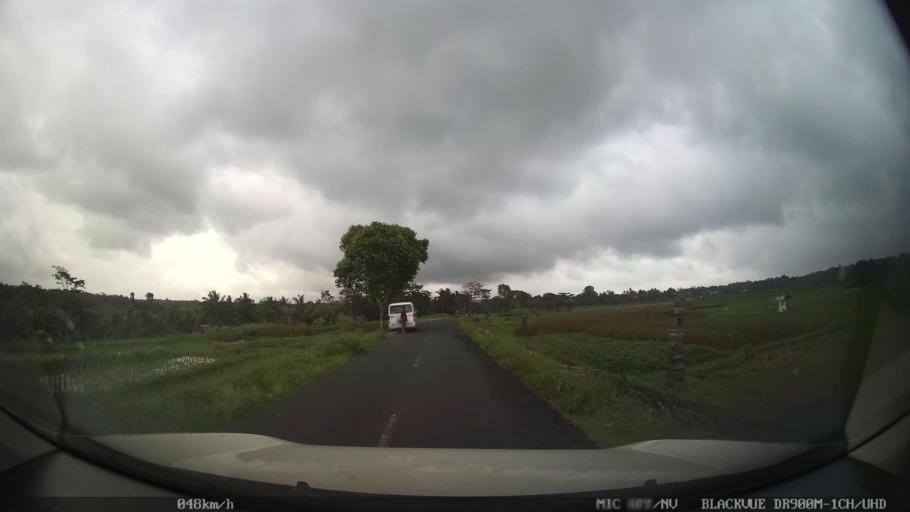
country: ID
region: Bali
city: Banjar Badung Tengah
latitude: -8.5166
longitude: 115.1958
